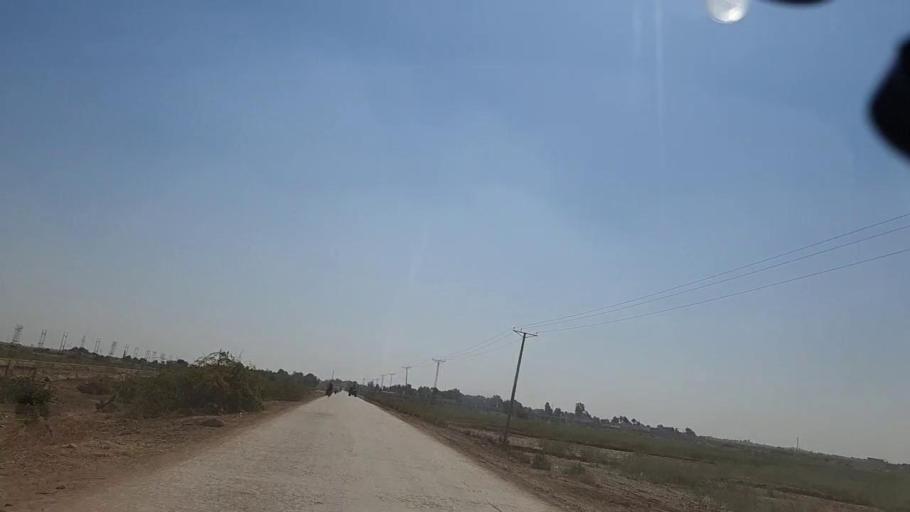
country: PK
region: Sindh
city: Mirpur Khas
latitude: 25.4928
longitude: 69.0389
